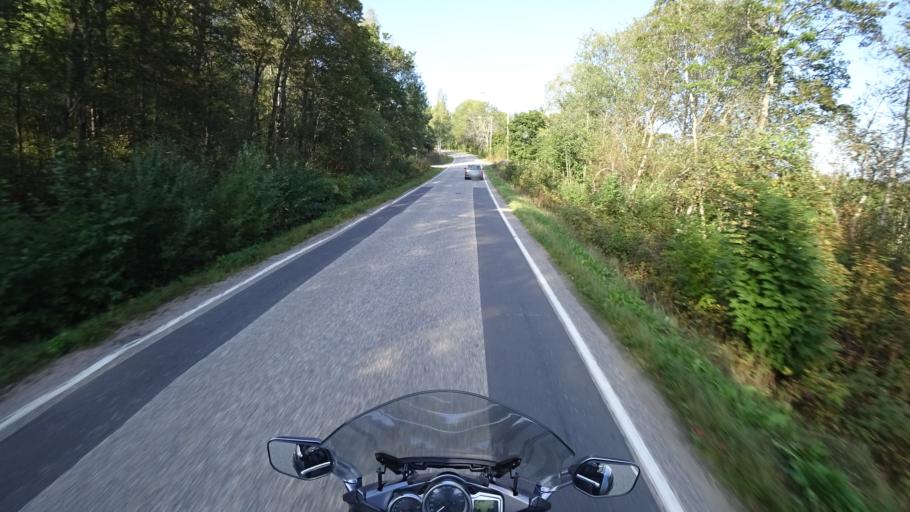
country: FI
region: Varsinais-Suomi
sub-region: Salo
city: Suomusjaervi
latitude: 60.3547
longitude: 23.6493
